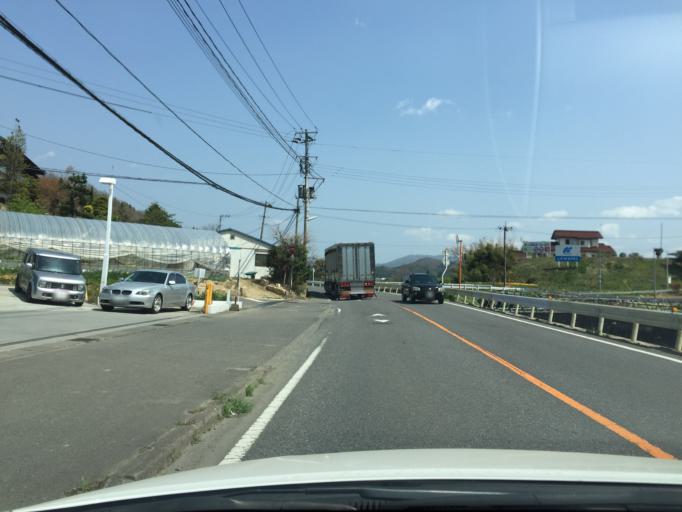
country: JP
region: Fukushima
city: Funehikimachi-funehiki
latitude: 37.4412
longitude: 140.6275
